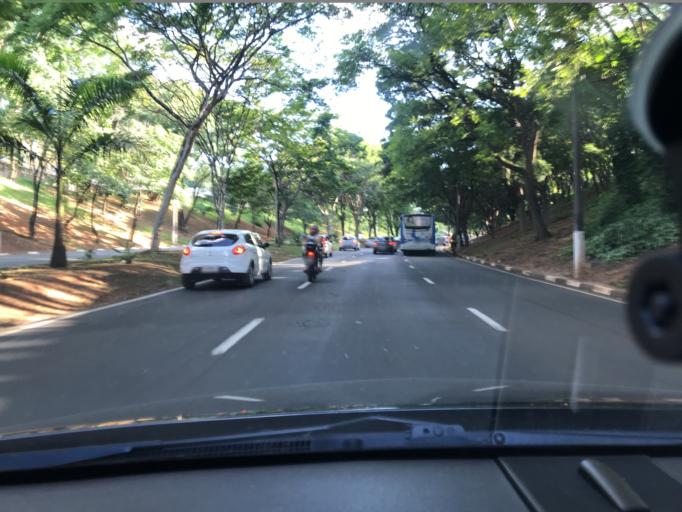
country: BR
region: Sao Paulo
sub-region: Campinas
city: Campinas
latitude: -22.9131
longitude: -47.0591
